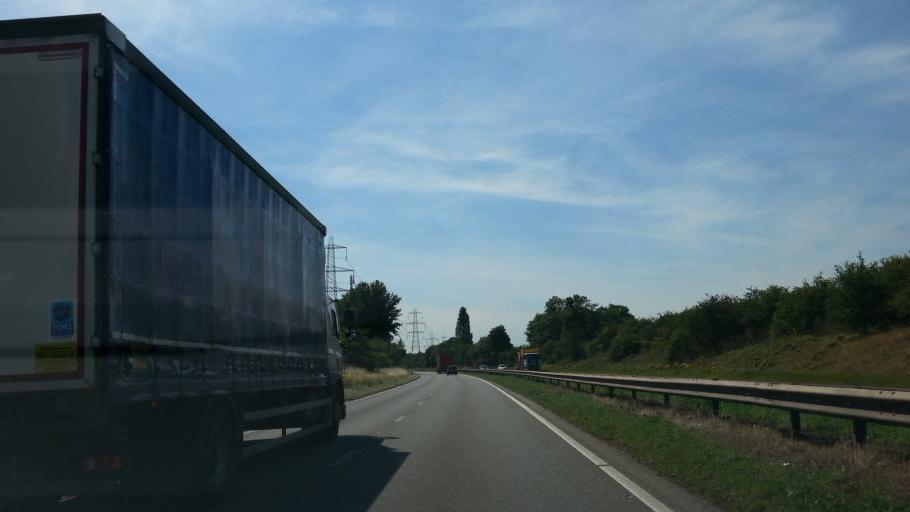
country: GB
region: England
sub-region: Staffordshire
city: Lichfield
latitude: 52.6697
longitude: -1.8091
